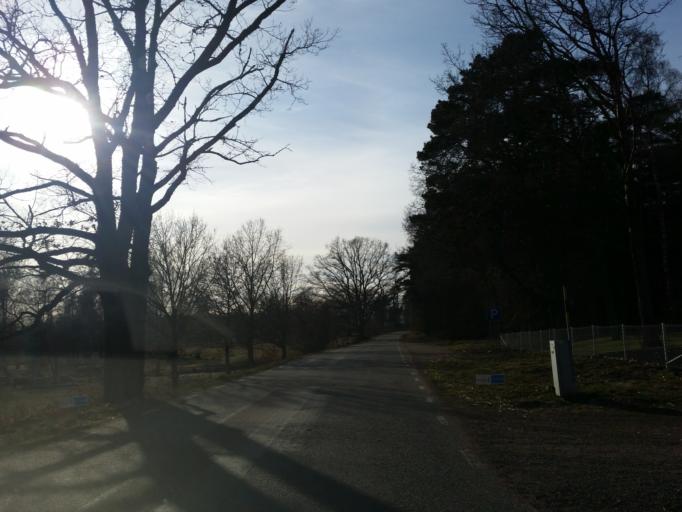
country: SE
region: Kalmar
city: Faerjestaden
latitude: 56.7741
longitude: 16.4634
